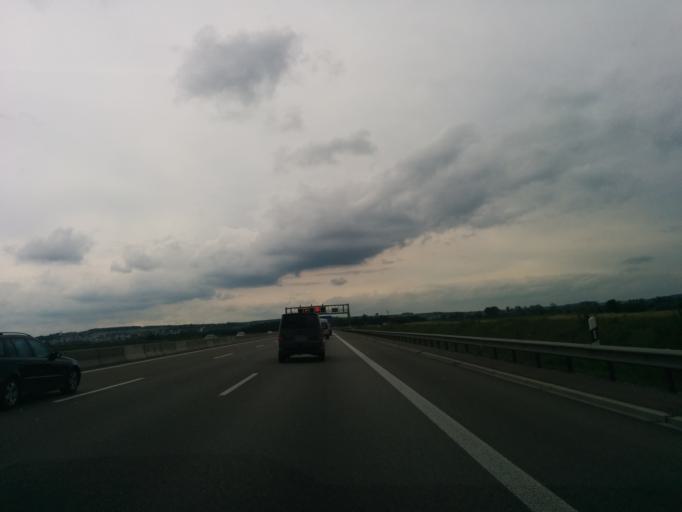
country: DE
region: Bavaria
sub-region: Swabia
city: Nersingen
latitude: 48.4622
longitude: 10.1446
